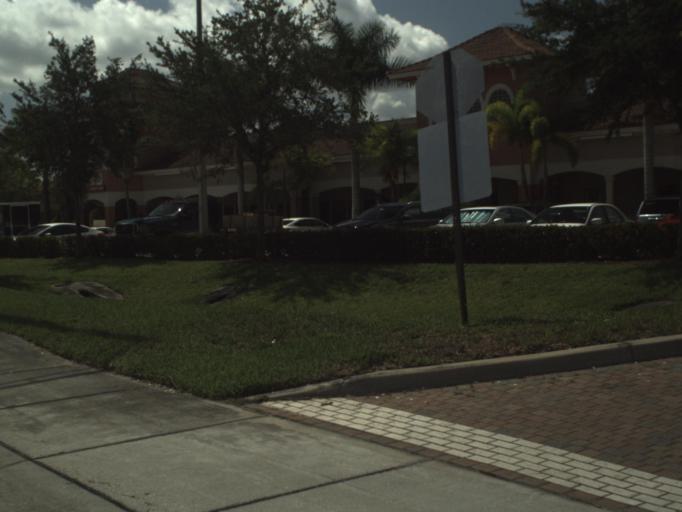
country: US
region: Florida
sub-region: Saint Lucie County
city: Port Saint Lucie
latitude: 27.2714
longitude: -80.3164
